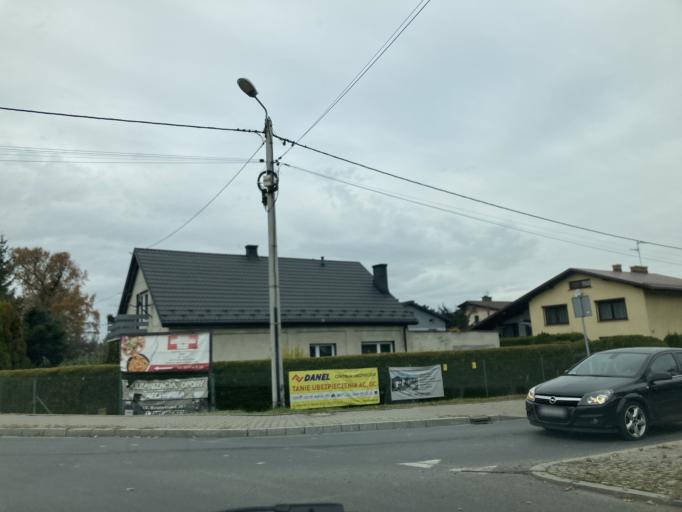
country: PL
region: Silesian Voivodeship
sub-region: Bielsko-Biala
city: Bielsko-Biala
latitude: 49.8574
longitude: 19.0486
